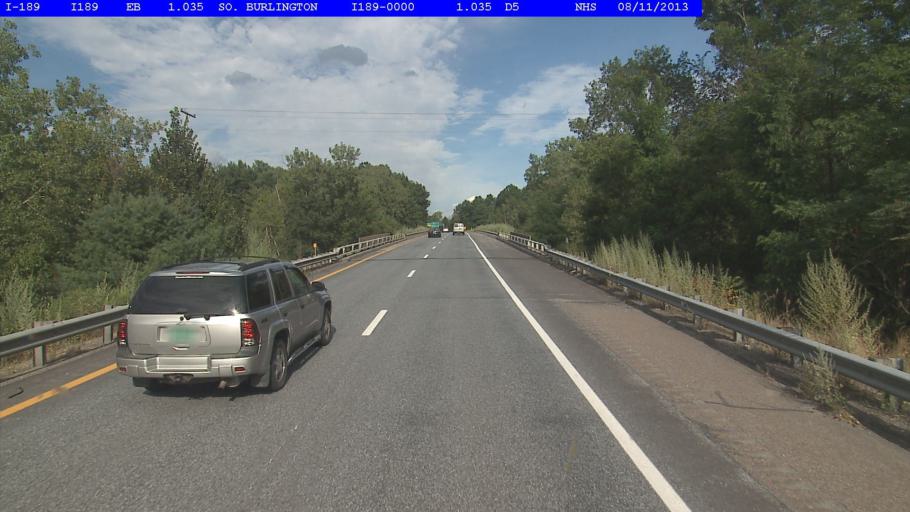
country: US
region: Vermont
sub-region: Chittenden County
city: South Burlington
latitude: 44.4499
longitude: -73.1890
